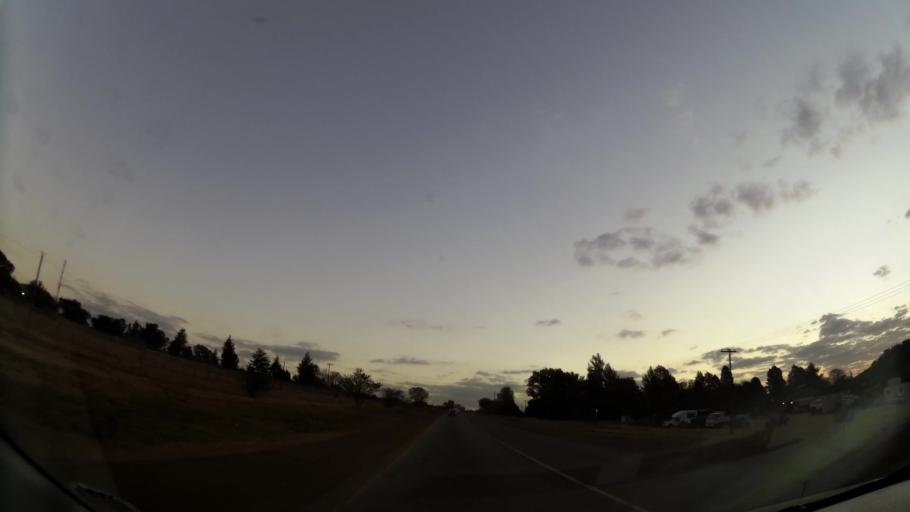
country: ZA
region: Gauteng
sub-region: West Rand District Municipality
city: Krugersdorp
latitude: -26.0673
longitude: 27.6892
